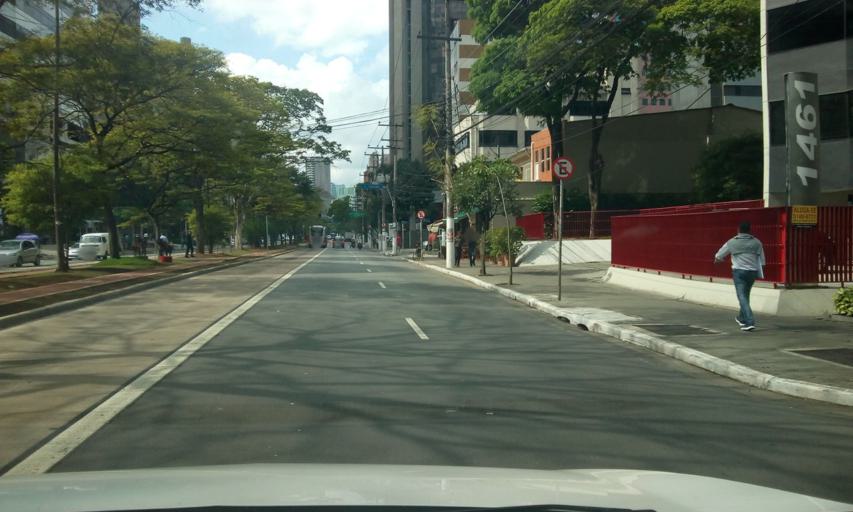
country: BR
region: Sao Paulo
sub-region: Sao Paulo
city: Sao Paulo
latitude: -23.6097
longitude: -46.6945
